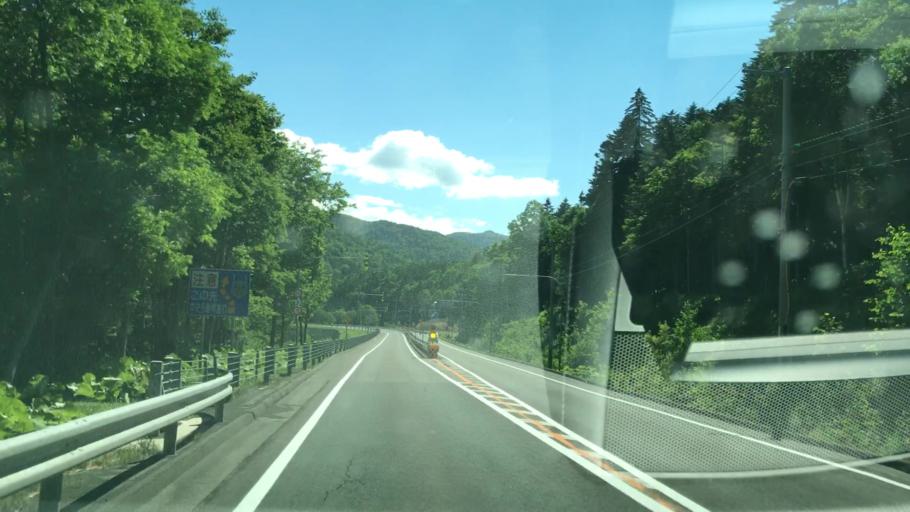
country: JP
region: Hokkaido
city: Shimo-furano
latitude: 42.9704
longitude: 142.6761
